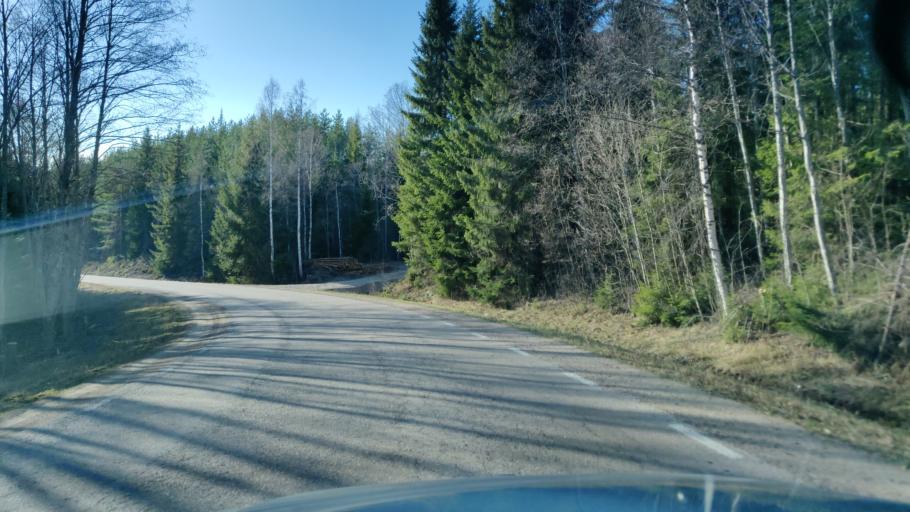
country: SE
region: Vaermland
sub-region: Munkfors Kommun
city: Munkfors
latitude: 59.9862
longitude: 13.3936
